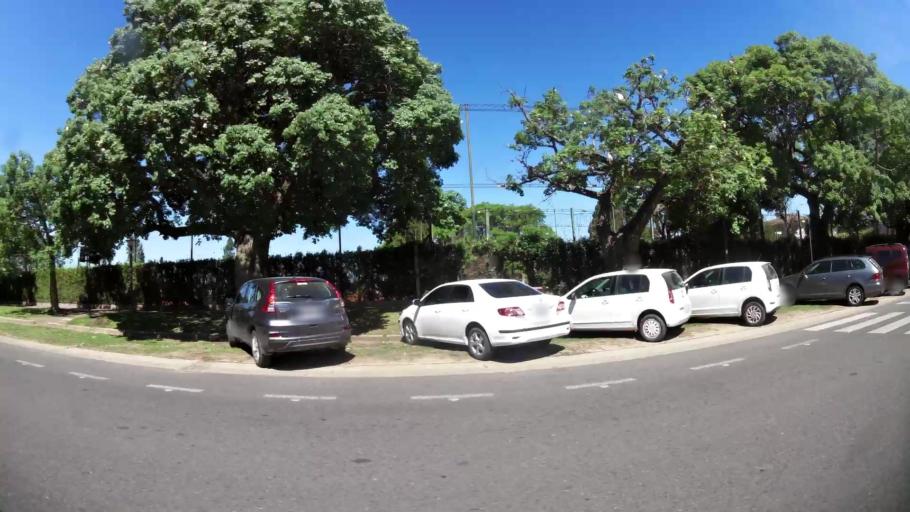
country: AR
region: Santa Fe
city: Santa Fe de la Vera Cruz
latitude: -31.6207
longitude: -60.6779
